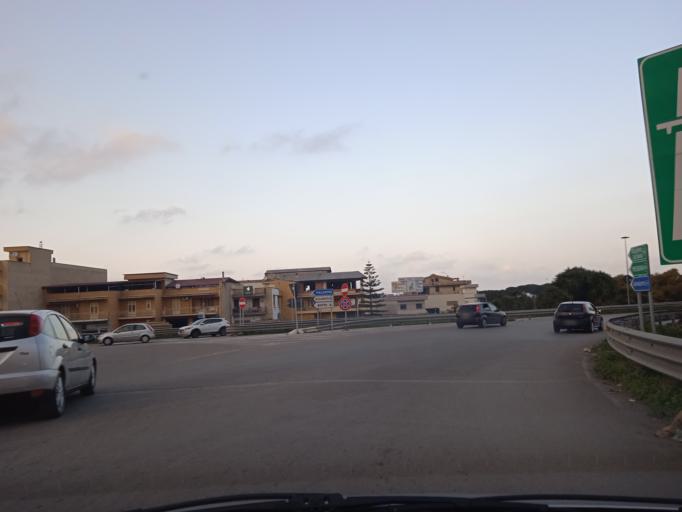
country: IT
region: Sicily
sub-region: Palermo
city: Villabate
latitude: 38.0813
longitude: 13.4355
